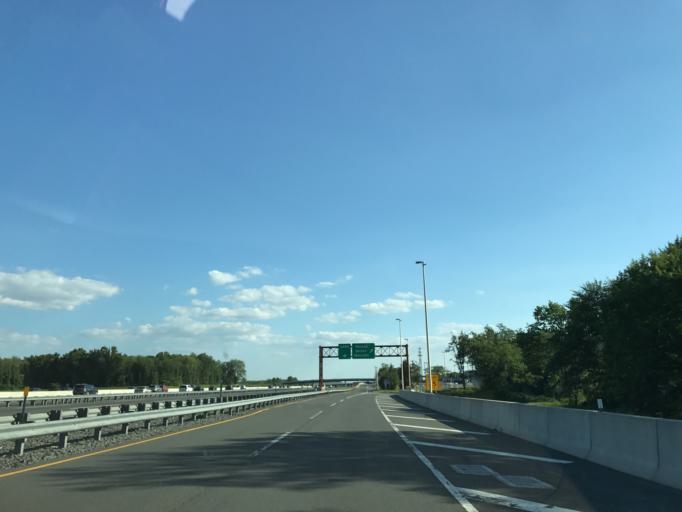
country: US
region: New Jersey
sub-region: Middlesex County
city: Rossmoor
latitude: 40.3244
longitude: -74.4855
